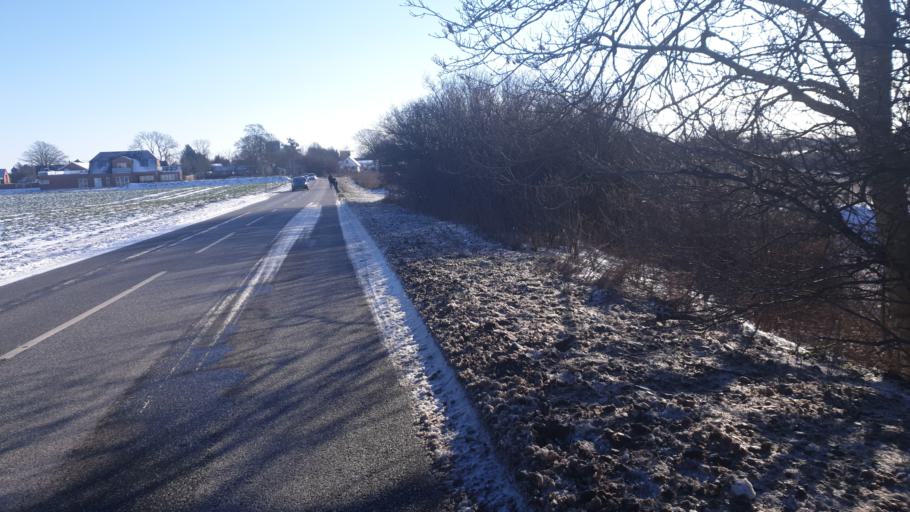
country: DK
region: Central Jutland
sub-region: Hedensted Kommune
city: Hedensted
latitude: 55.7837
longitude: 9.7103
